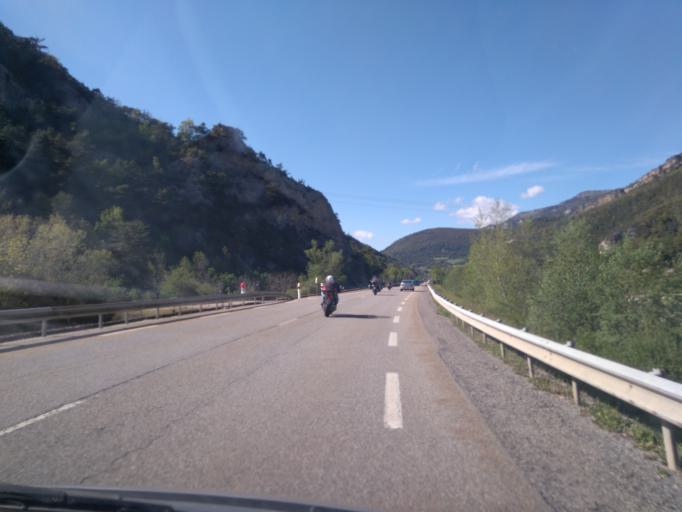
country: FR
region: Provence-Alpes-Cote d'Azur
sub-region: Departement des Hautes-Alpes
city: Veynes
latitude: 44.5968
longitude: 5.7095
